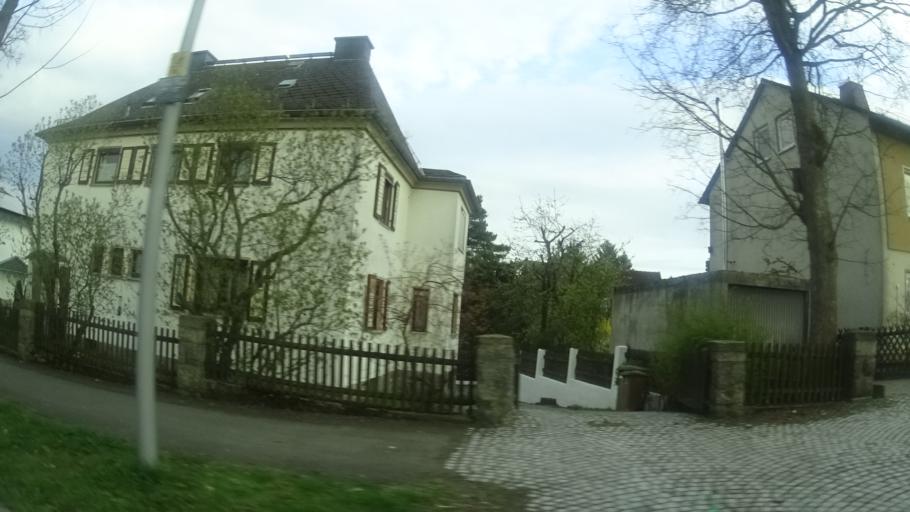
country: DE
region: Bavaria
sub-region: Upper Franconia
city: Hof
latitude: 50.3046
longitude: 11.9036
